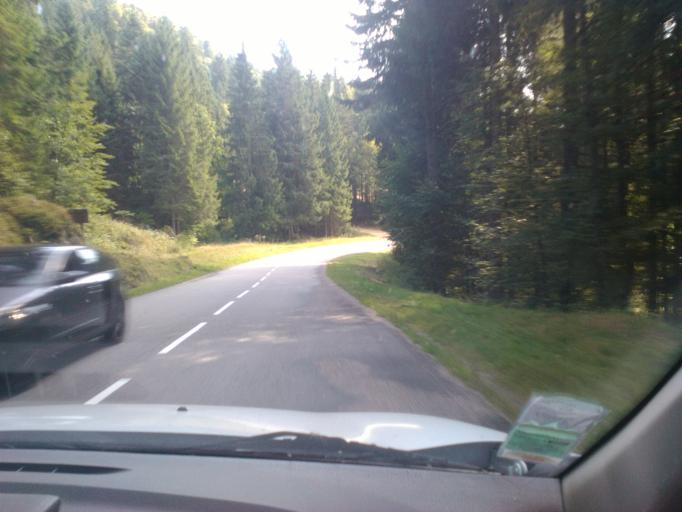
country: FR
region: Lorraine
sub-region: Departement des Vosges
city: Xonrupt-Longemer
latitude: 48.0448
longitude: 6.9339
